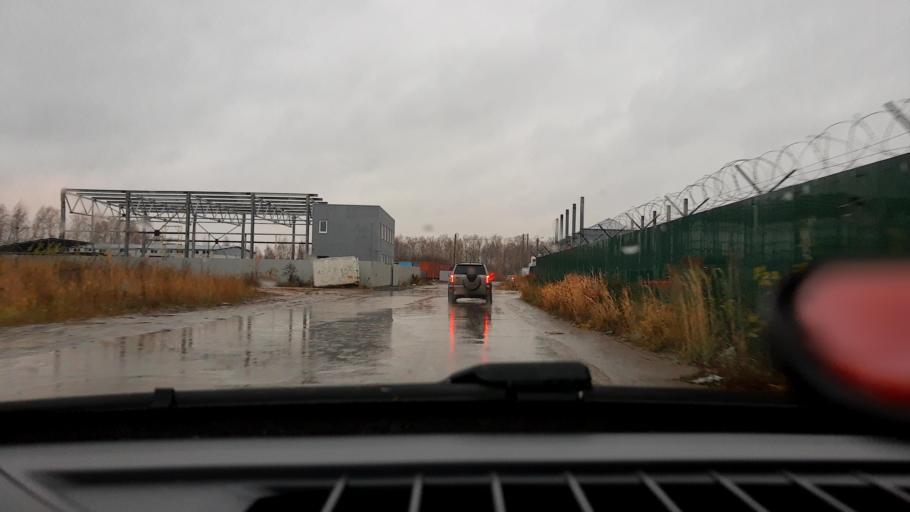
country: RU
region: Nizjnij Novgorod
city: Gorbatovka
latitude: 56.3157
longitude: 43.8512
